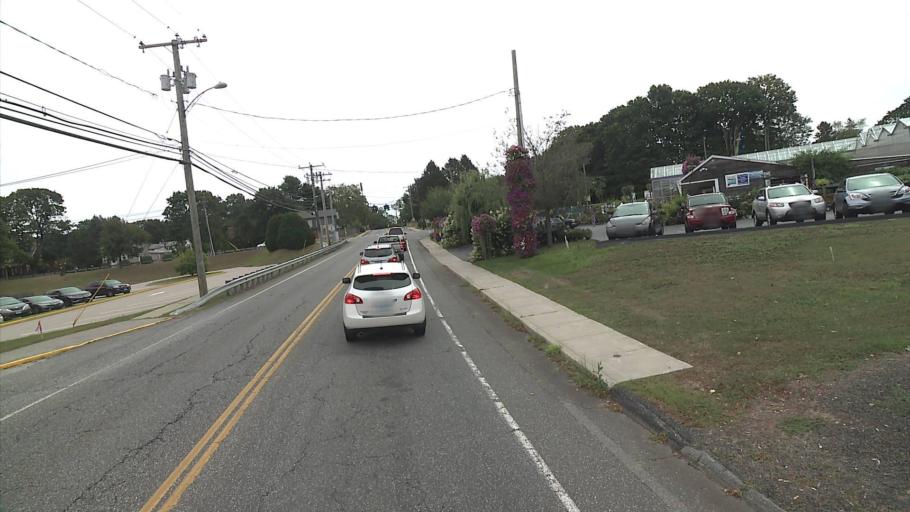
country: US
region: Connecticut
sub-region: New London County
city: Niantic
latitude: 41.3222
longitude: -72.2037
